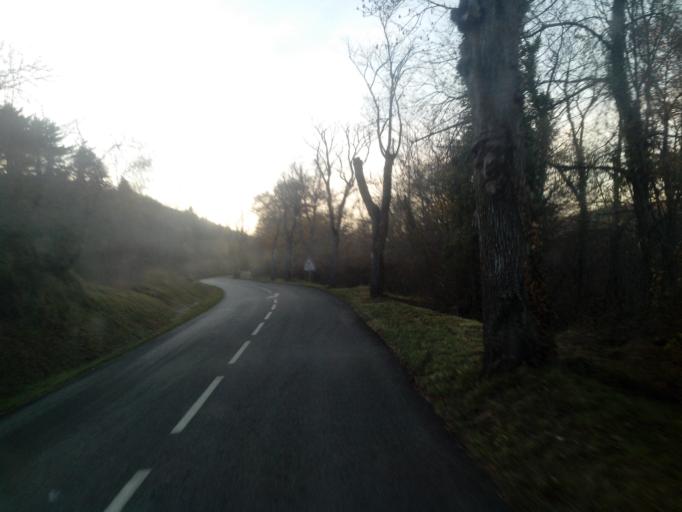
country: FR
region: Languedoc-Roussillon
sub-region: Departement de l'Aude
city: Chalabre
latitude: 42.9099
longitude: 2.0068
